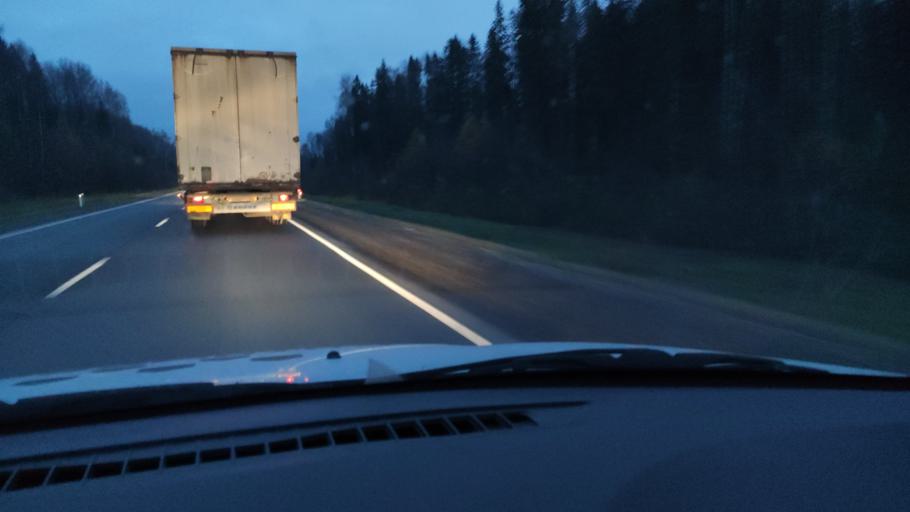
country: RU
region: Kirov
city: Kostino
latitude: 58.8336
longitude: 53.4793
